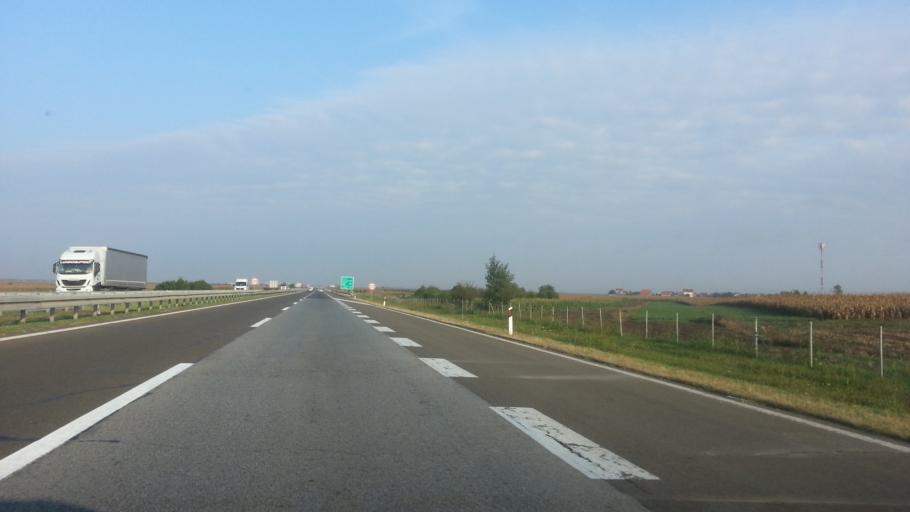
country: RS
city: Novi Banovci
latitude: 44.9458
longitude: 20.2776
